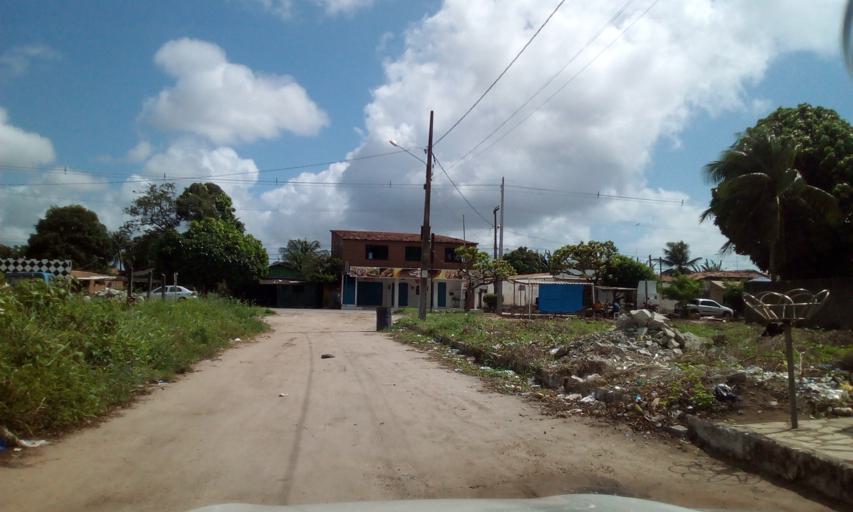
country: BR
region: Paraiba
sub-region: Conde
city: Conde
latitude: -7.2164
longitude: -34.8320
